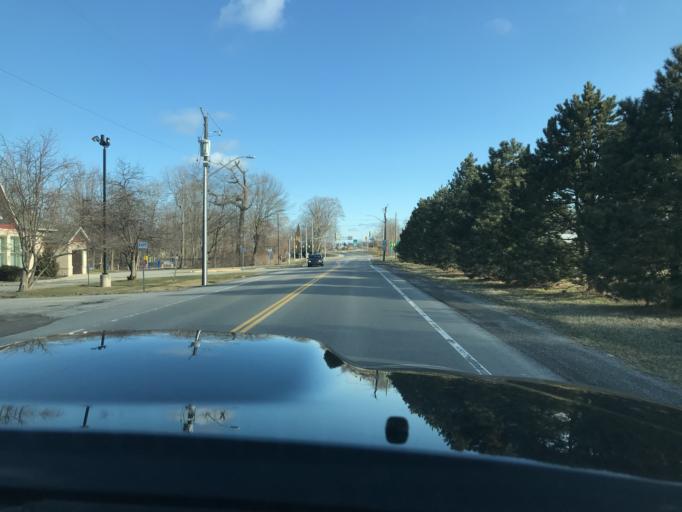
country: CA
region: Ontario
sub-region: Regional Municipality of Niagara
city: St. Catharines
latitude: 43.1751
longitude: -79.3087
